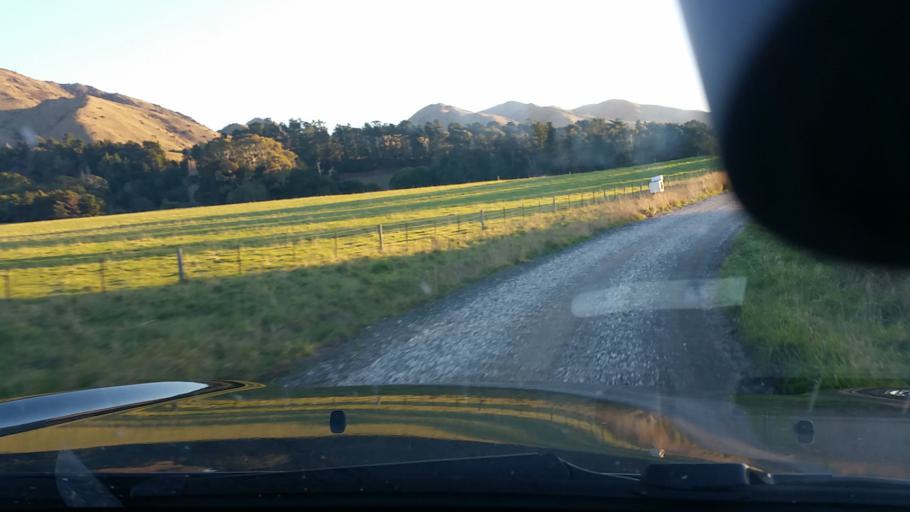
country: NZ
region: Marlborough
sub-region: Marlborough District
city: Blenheim
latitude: -41.7384
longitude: 174.0476
